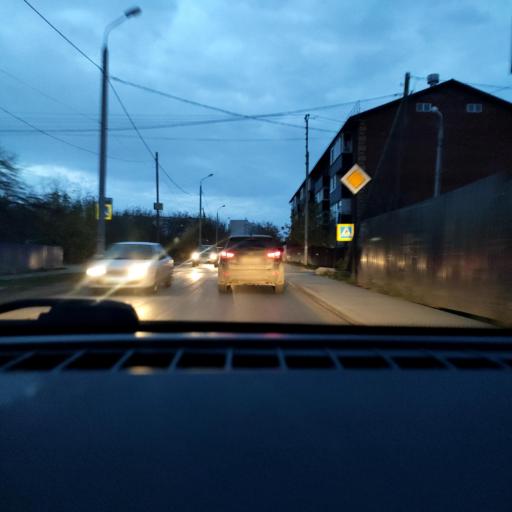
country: RU
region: Perm
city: Perm
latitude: 57.9736
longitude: 56.1937
